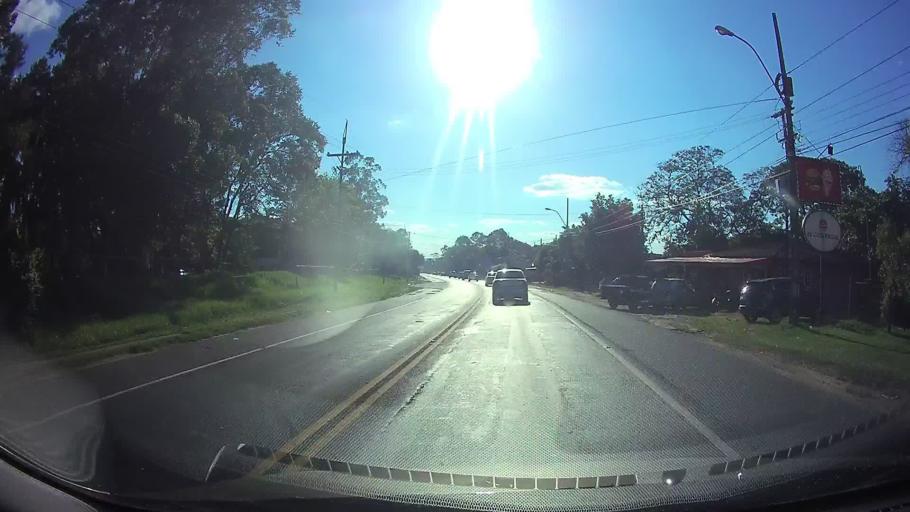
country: PY
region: Central
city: Ypacarai
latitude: -25.3729
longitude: -57.2218
